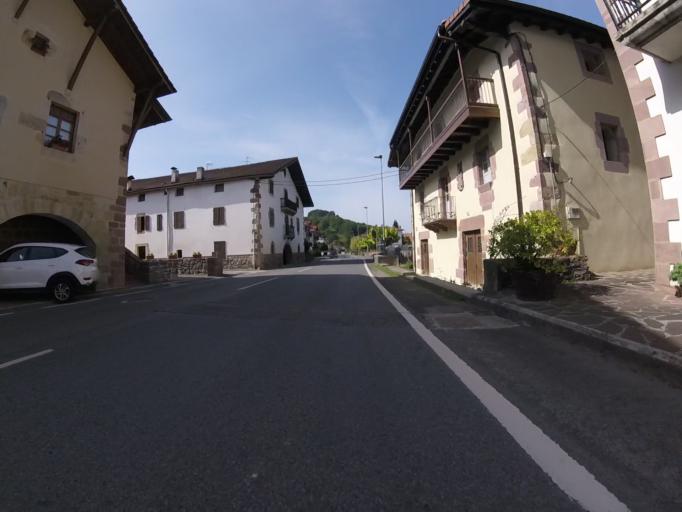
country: ES
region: Navarre
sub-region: Provincia de Navarra
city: Doneztebe
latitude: 43.1397
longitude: -1.6068
